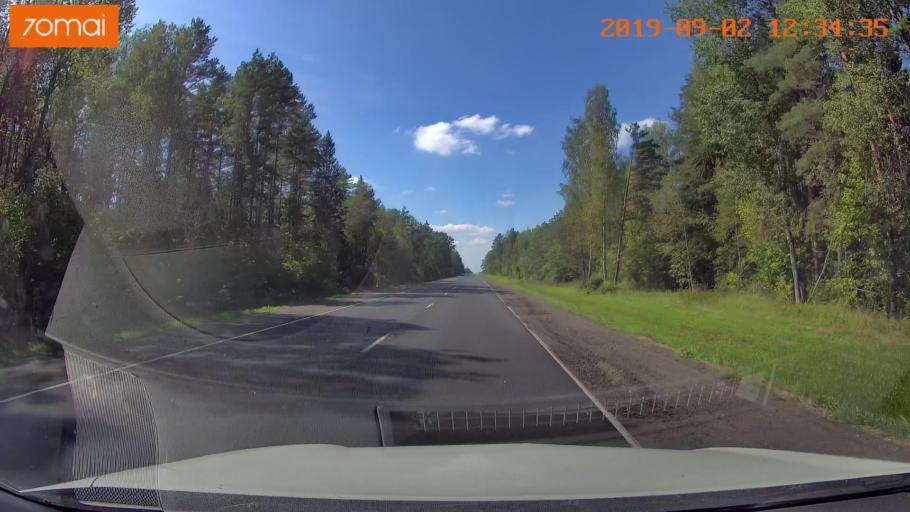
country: RU
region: Smolensk
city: Shumyachi
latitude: 53.8092
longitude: 32.4008
